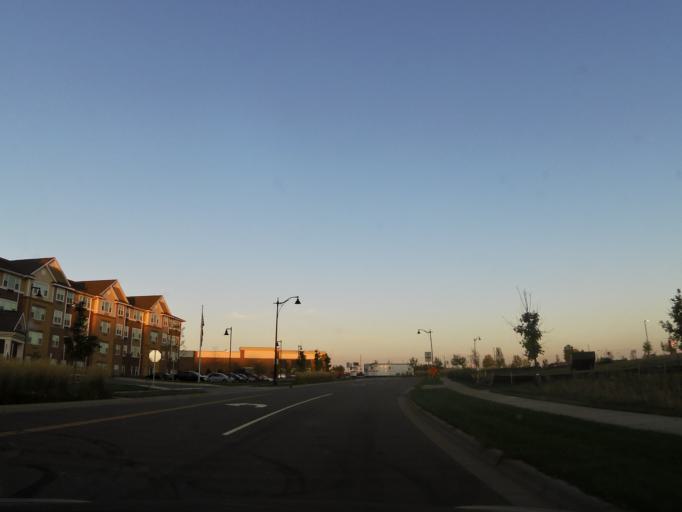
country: US
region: Minnesota
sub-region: Washington County
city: Oakdale
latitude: 44.9648
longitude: -92.9631
